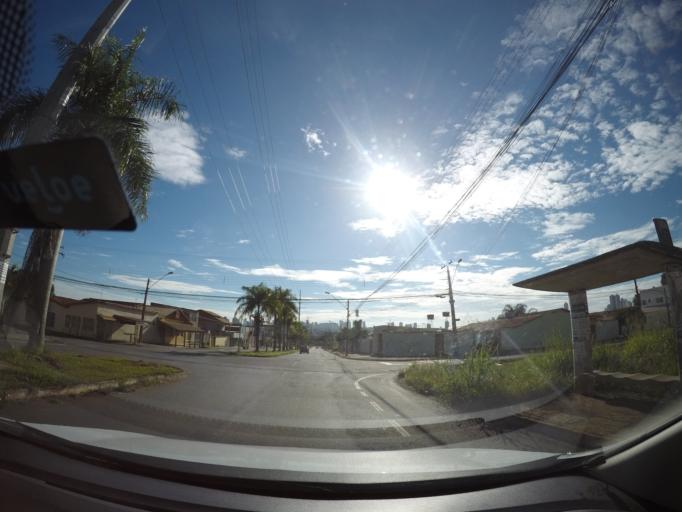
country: BR
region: Goias
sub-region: Goiania
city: Goiania
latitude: -16.7254
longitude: -49.2991
